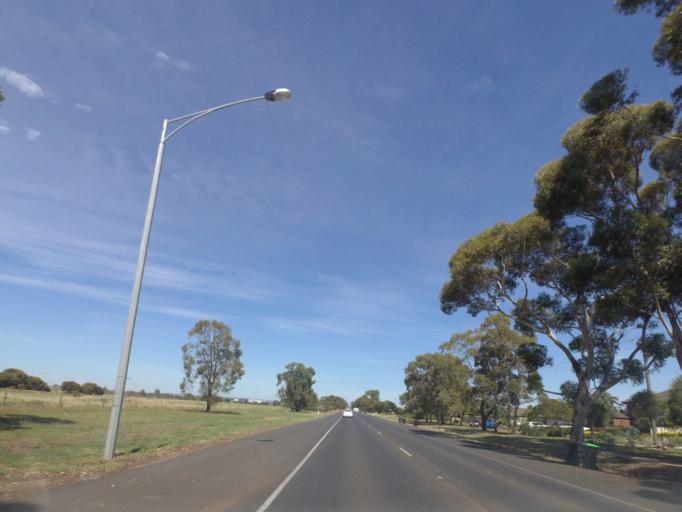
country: AU
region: Victoria
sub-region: Melton
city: Brookfield
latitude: -37.6857
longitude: 144.5484
